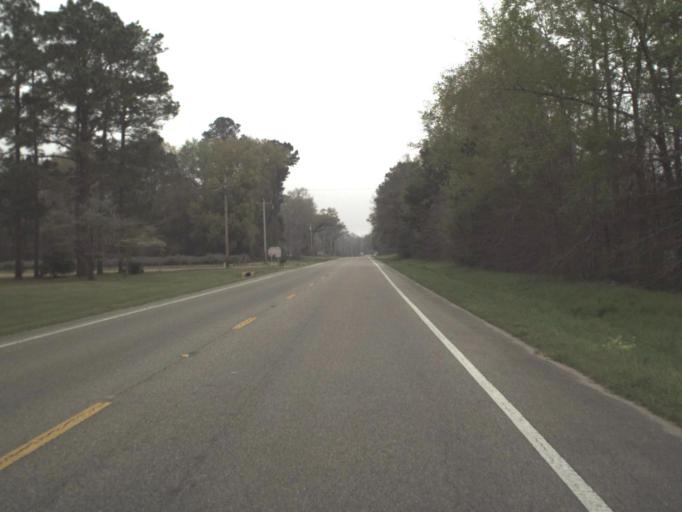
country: US
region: Florida
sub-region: Gadsden County
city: Gretna
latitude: 30.5788
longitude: -84.6728
